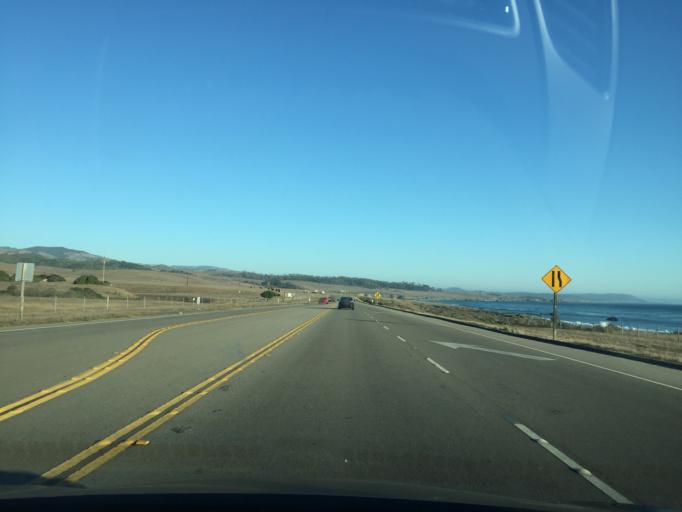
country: US
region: California
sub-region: San Luis Obispo County
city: Cambria
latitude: 35.6434
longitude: -121.1843
